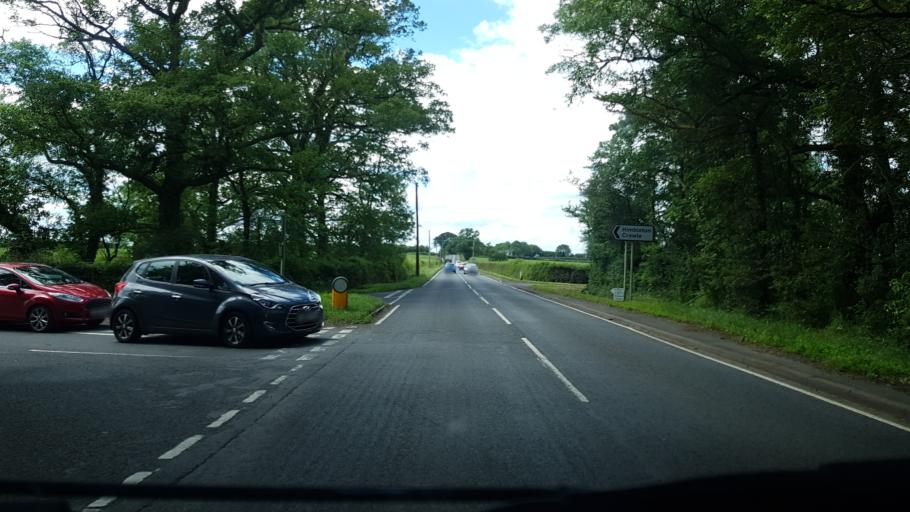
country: GB
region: England
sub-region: Worcestershire
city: Droitwich
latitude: 52.2629
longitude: -2.1004
